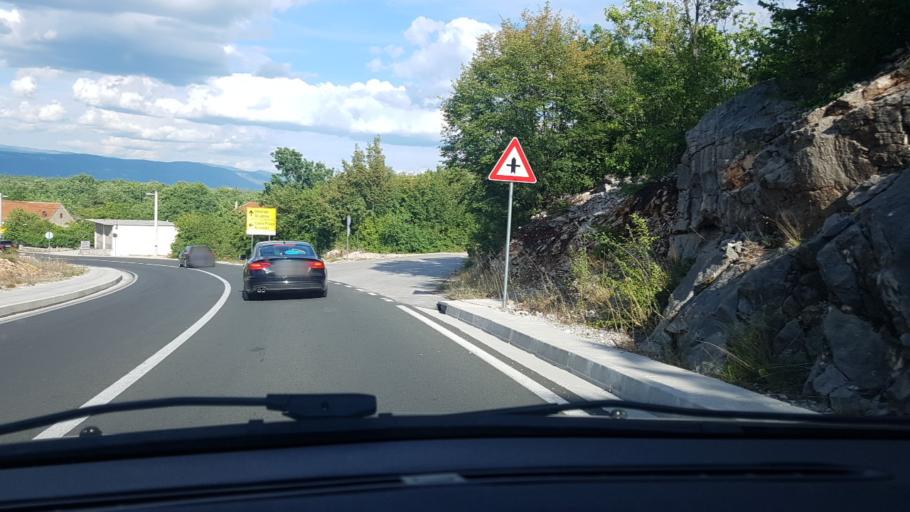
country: HR
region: Splitsko-Dalmatinska
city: Grubine
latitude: 43.4237
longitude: 17.1277
